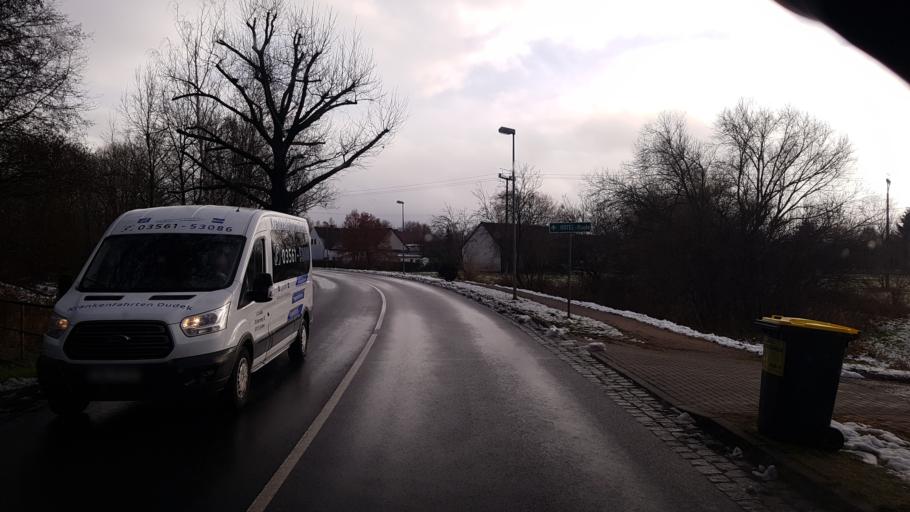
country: DE
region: Brandenburg
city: Forst
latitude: 51.8057
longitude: 14.6005
